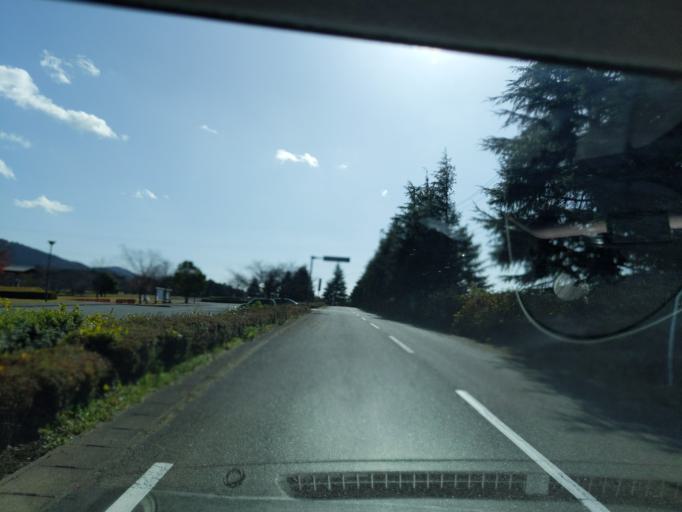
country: JP
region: Iwate
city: Mizusawa
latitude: 39.0270
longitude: 141.1231
